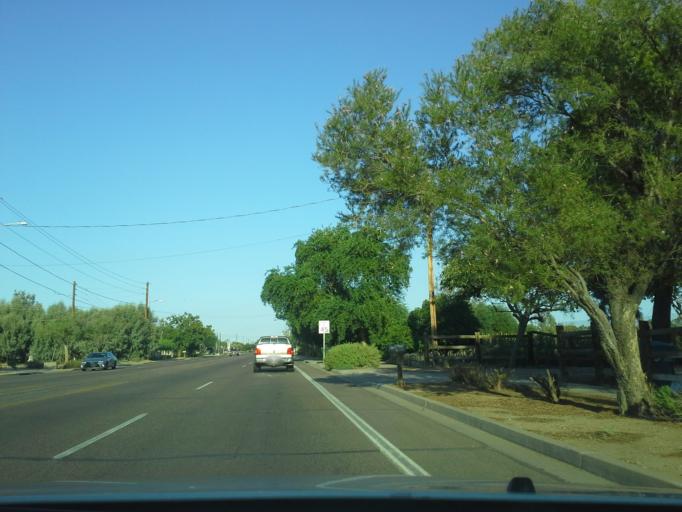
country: US
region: Arizona
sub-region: Maricopa County
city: Guadalupe
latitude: 33.3926
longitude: -112.0078
